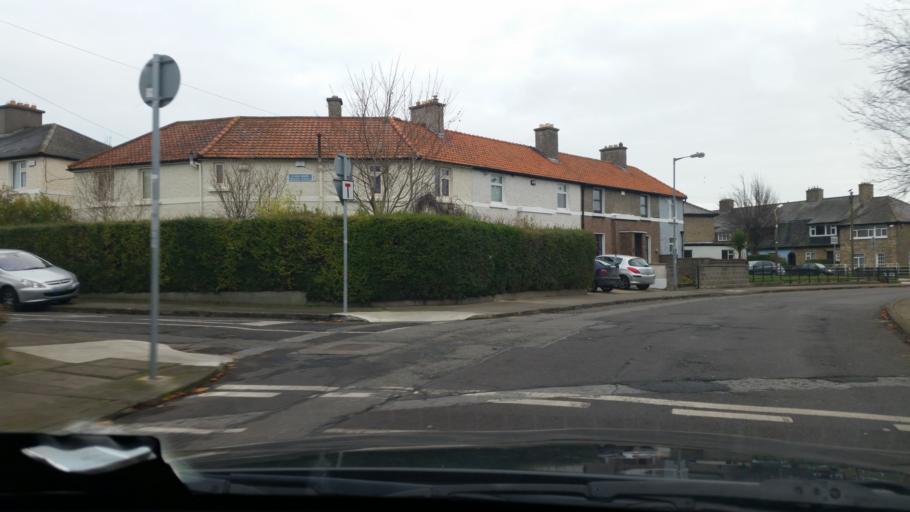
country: IE
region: Leinster
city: Marino
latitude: 53.3671
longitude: -6.2337
